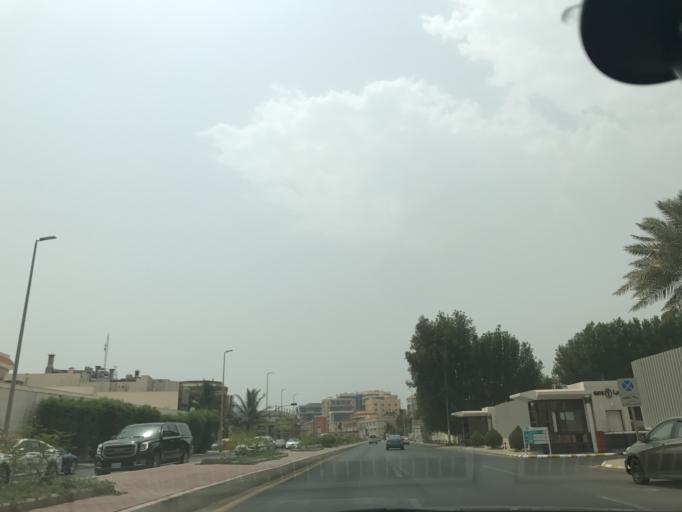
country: SA
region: Makkah
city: Jeddah
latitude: 21.5582
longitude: 39.1476
